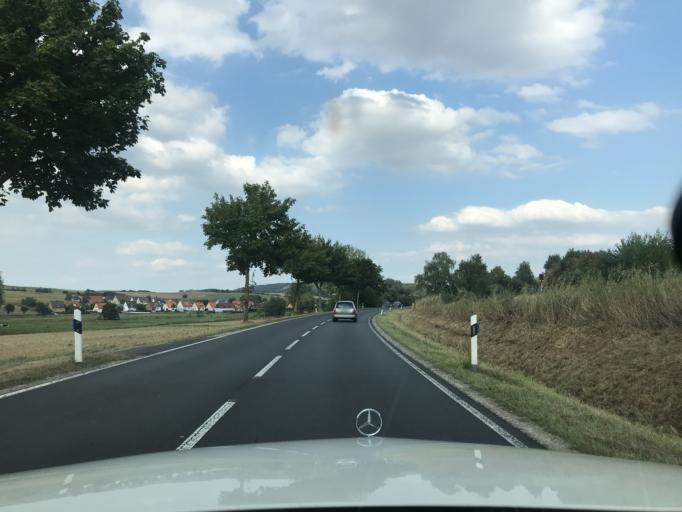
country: DE
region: Lower Saxony
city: Adelebsen
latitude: 51.5931
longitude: 9.7703
